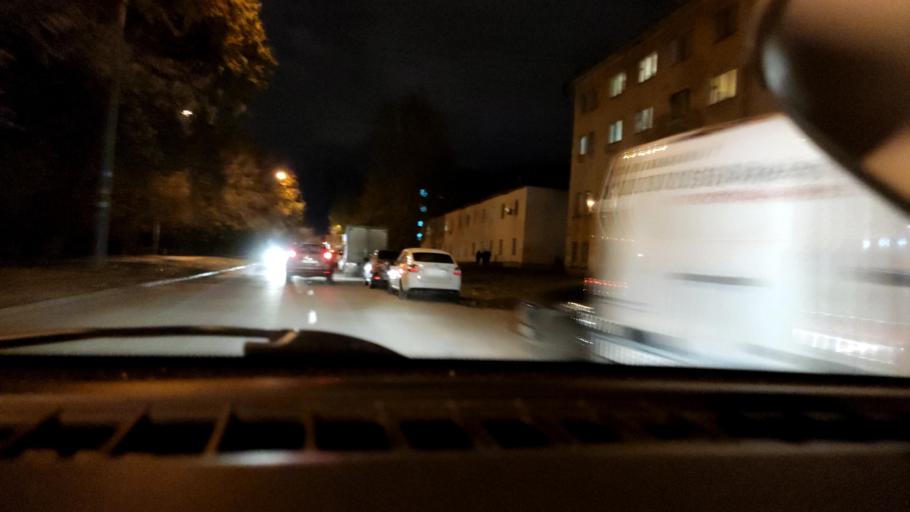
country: RU
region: Samara
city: Samara
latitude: 53.2089
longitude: 50.1807
